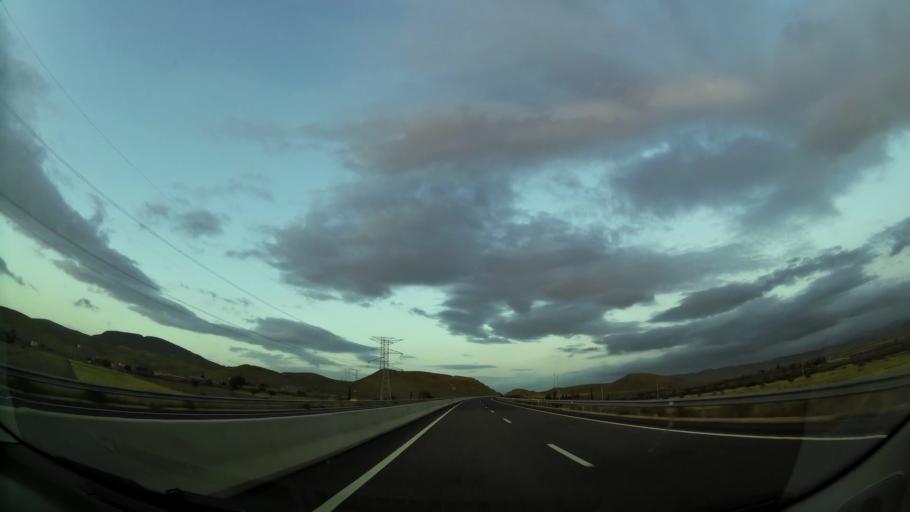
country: MA
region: Oriental
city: El Aioun
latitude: 34.5949
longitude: -2.6778
